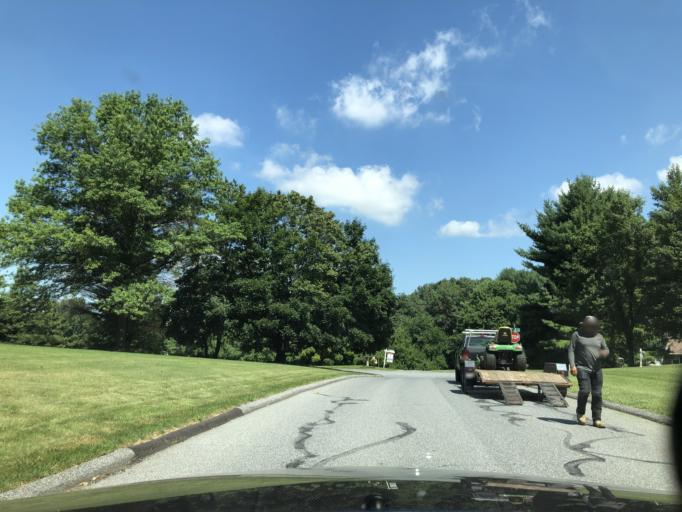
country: US
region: Maryland
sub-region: Carroll County
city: Westminster
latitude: 39.6203
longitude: -77.0018
